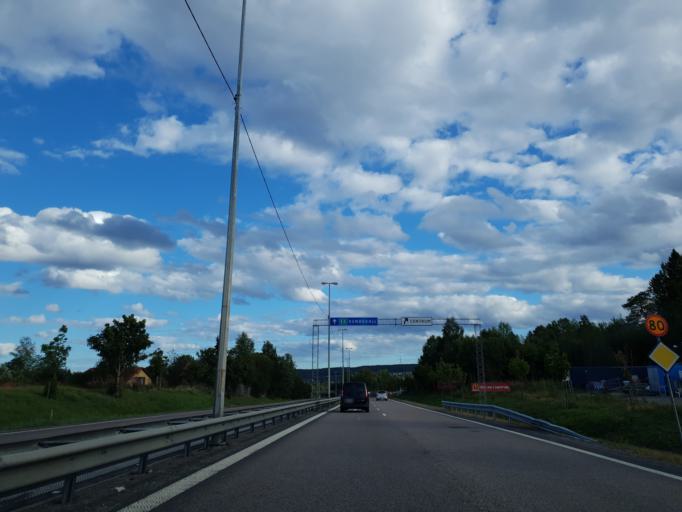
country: SE
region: Vaesternorrland
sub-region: Haernoesands Kommun
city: Haernoesand
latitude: 62.6427
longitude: 17.9111
